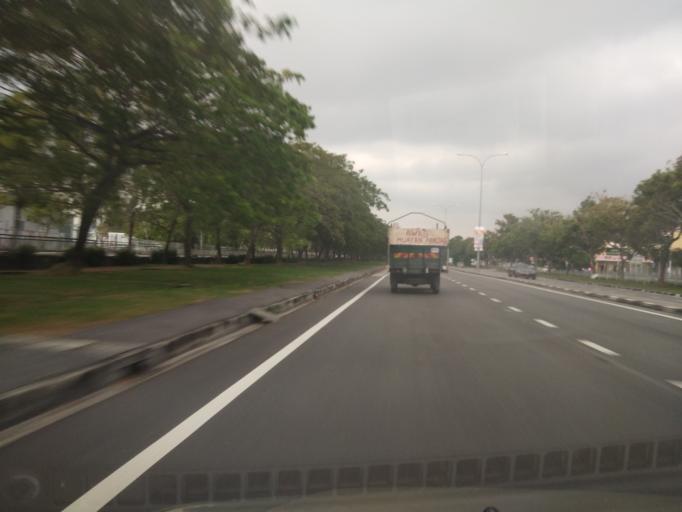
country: MY
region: Penang
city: Tasek Glugor
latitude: 5.5199
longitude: 100.4779
